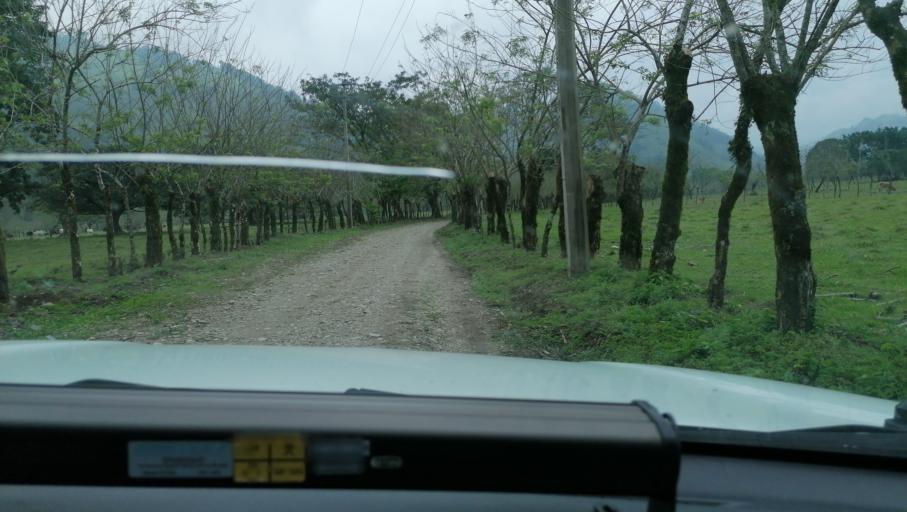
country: MX
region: Chiapas
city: Ixtacomitan
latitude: 17.3653
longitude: -93.1763
